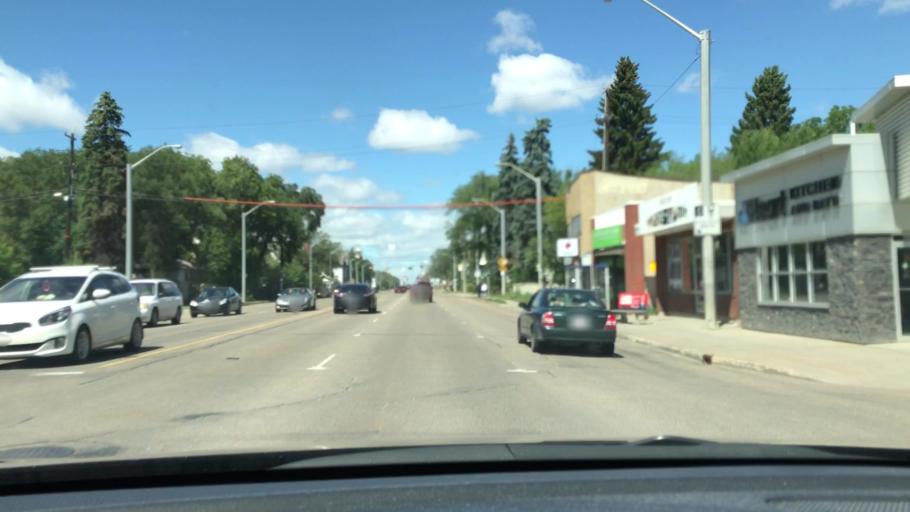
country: CA
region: Alberta
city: Edmonton
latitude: 53.5142
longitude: -113.5119
